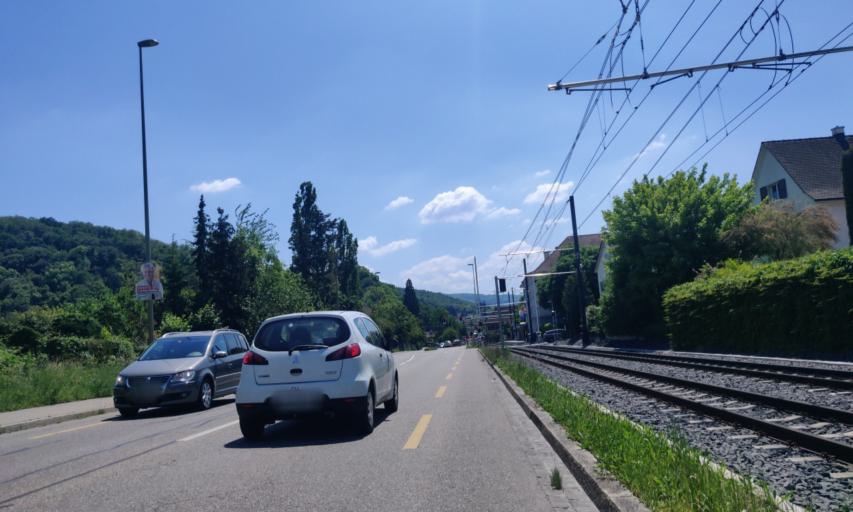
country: CH
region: Basel-Landschaft
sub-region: Bezirk Arlesheim
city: Munchenstein
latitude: 47.5210
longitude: 7.6180
